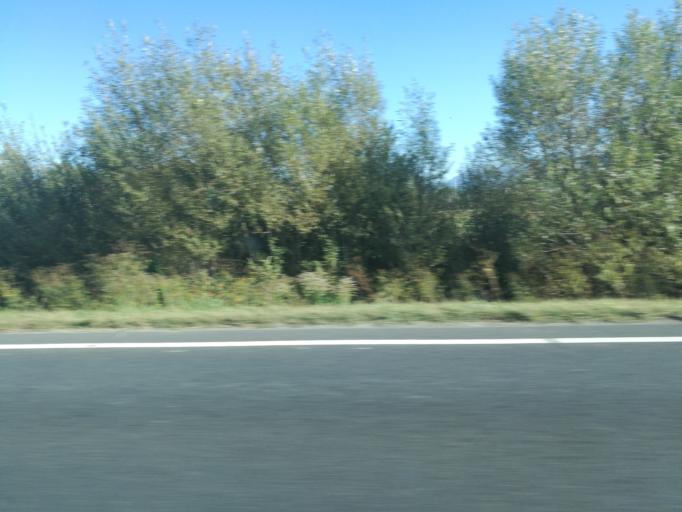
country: RO
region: Brasov
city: Brasov
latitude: 45.6830
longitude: 25.5601
